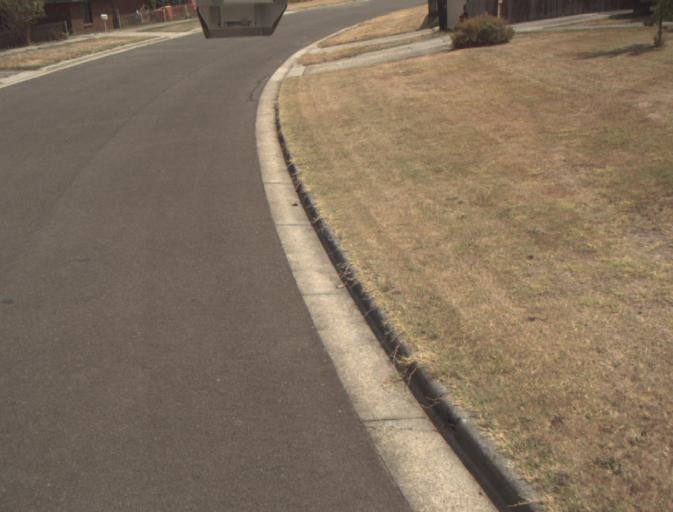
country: AU
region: Tasmania
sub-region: Launceston
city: Mayfield
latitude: -41.3845
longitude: 147.1220
